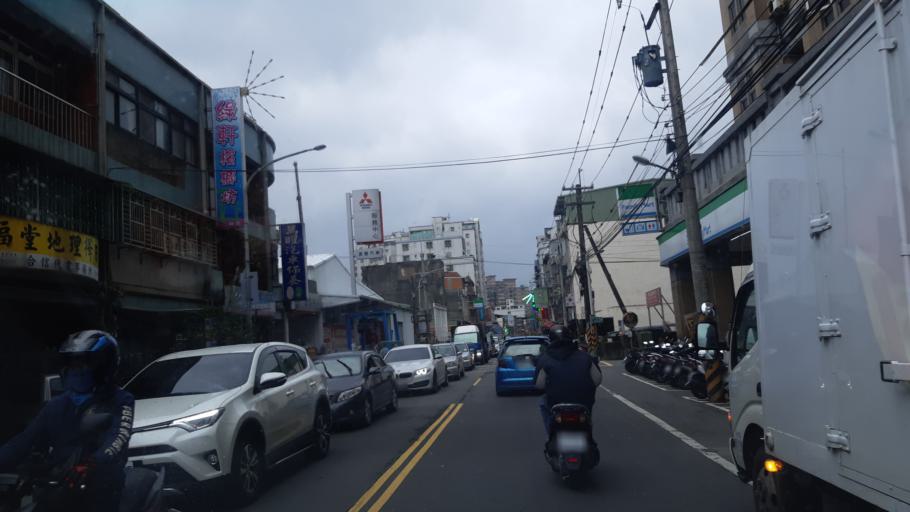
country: TW
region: Taiwan
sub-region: Taoyuan
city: Taoyuan
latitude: 24.9379
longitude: 121.3611
